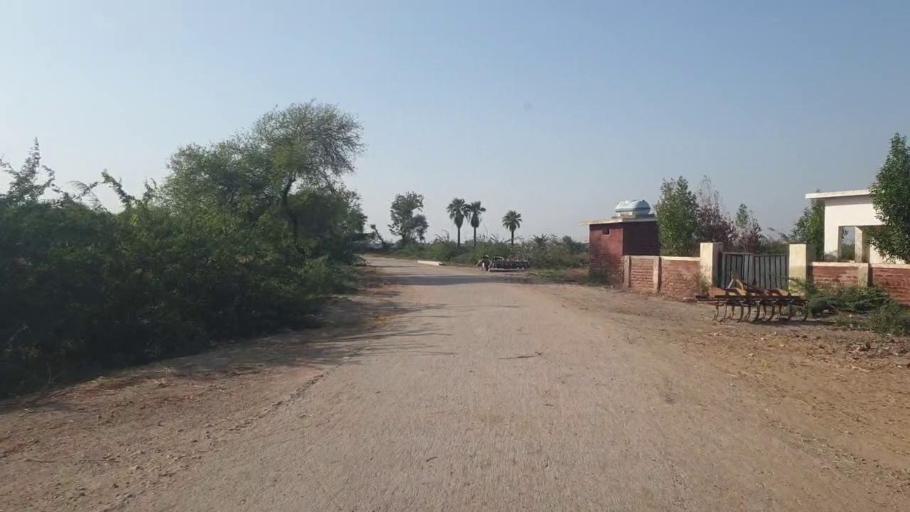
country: PK
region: Sindh
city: Badin
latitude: 24.6574
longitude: 68.8111
